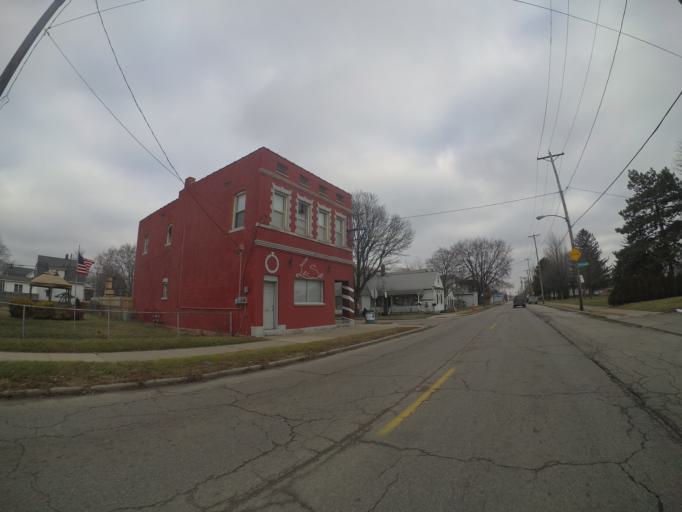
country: US
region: Ohio
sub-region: Lucas County
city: Oregon
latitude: 41.6436
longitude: -83.5093
